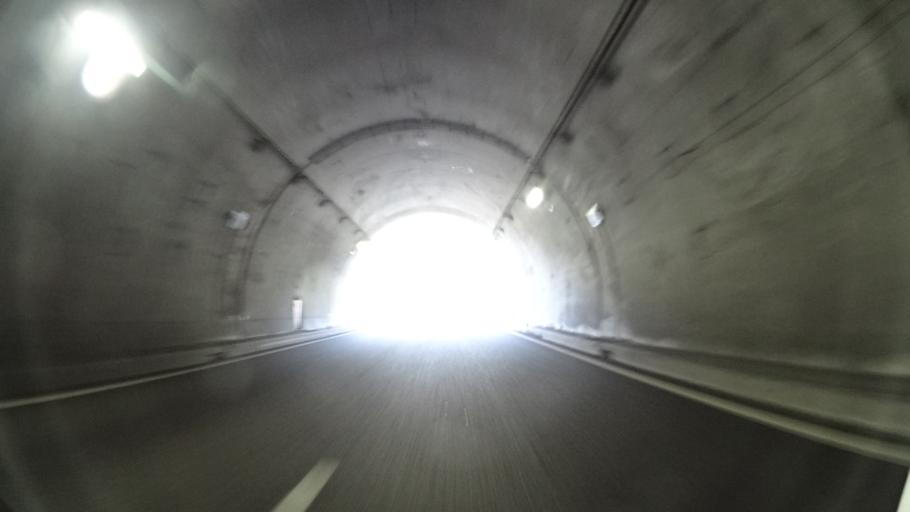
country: JP
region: Ehime
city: Saijo
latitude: 33.8863
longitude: 133.1553
